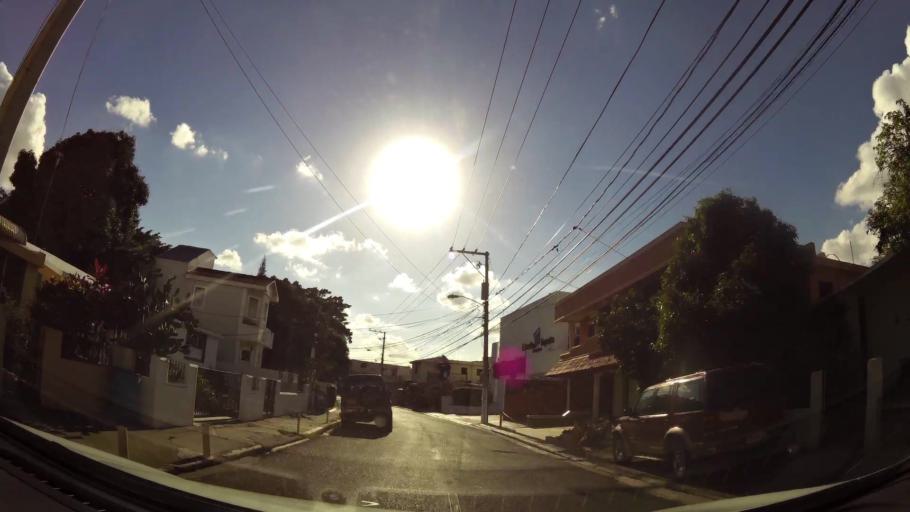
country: DO
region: Santiago
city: Santiago de los Caballeros
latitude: 19.4646
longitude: -70.6904
